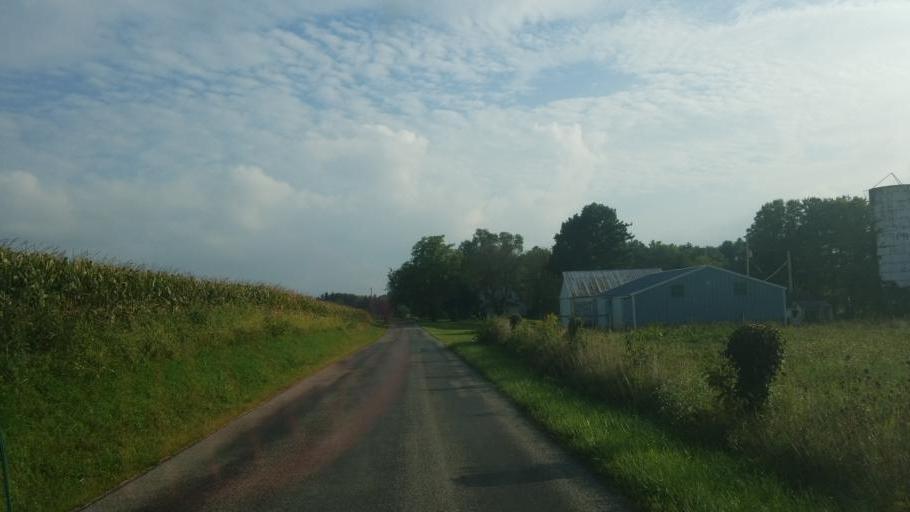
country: US
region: Ohio
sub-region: Wayne County
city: Wooster
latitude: 40.8822
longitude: -82.0216
